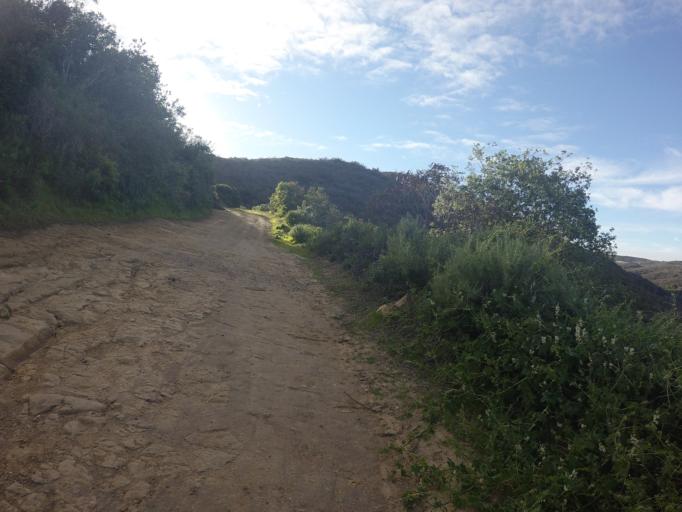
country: US
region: California
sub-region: Orange County
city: Aliso Viejo
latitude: 33.5884
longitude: -117.7684
